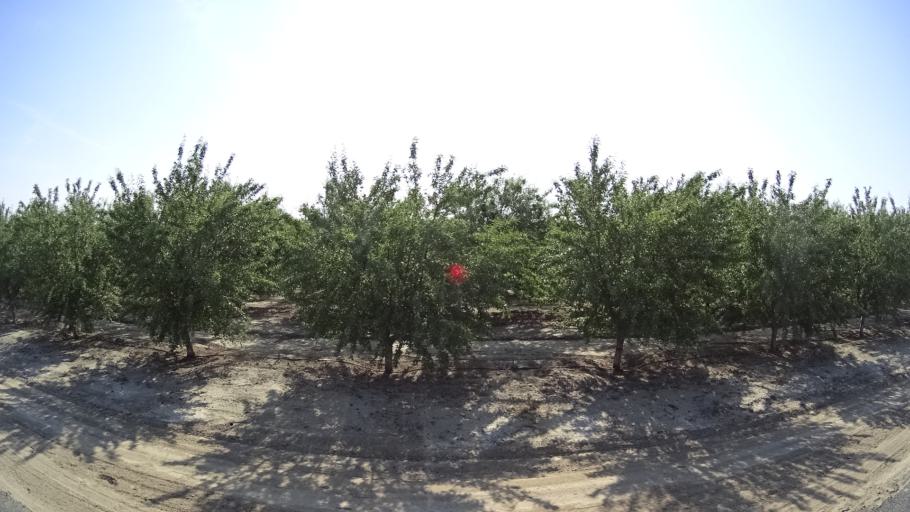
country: US
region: California
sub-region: Kings County
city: Lemoore
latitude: 36.3423
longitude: -119.8339
